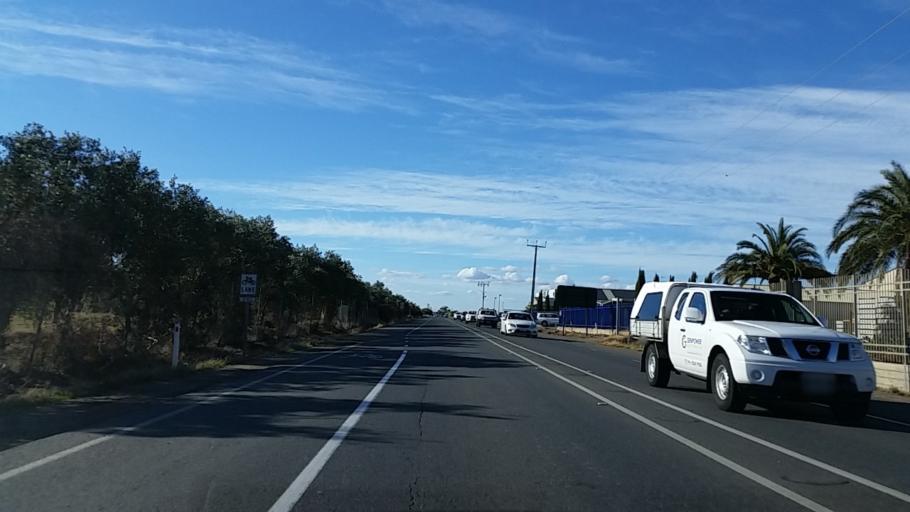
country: AU
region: South Australia
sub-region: Salisbury
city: Salisbury
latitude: -34.7307
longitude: 138.5905
